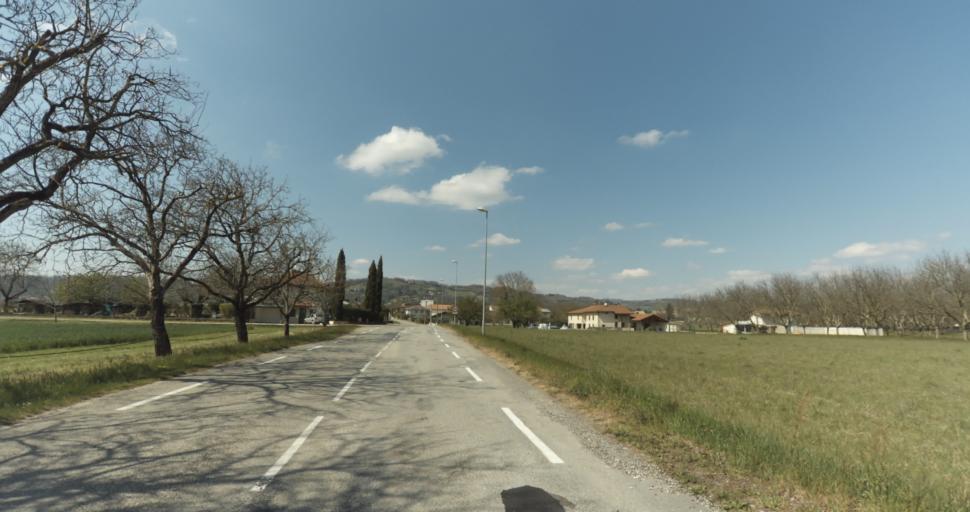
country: FR
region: Rhone-Alpes
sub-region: Departement de l'Isere
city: Saint-Marcellin
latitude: 45.1401
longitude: 5.3216
